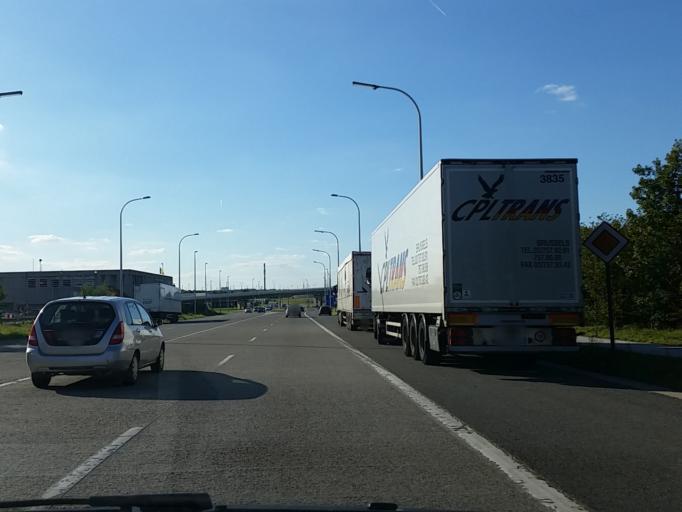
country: BE
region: Flanders
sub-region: Provincie Vlaams-Brabant
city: Machelen
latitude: 50.9091
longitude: 4.4674
